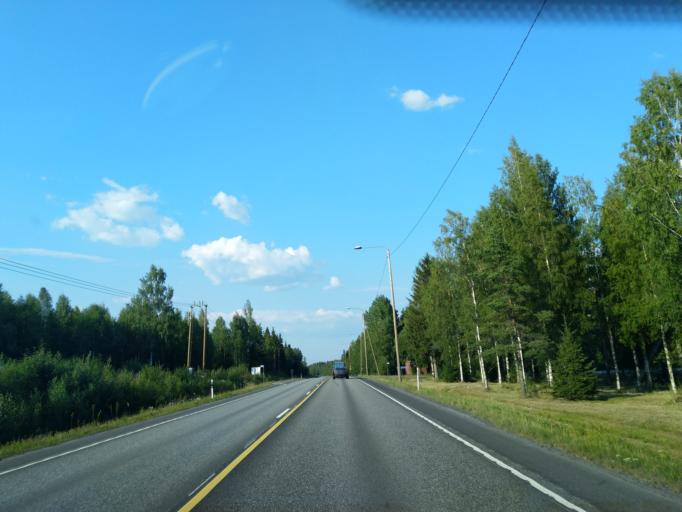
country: FI
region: Satakunta
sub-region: Pori
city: Pomarkku
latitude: 61.7066
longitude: 22.0258
